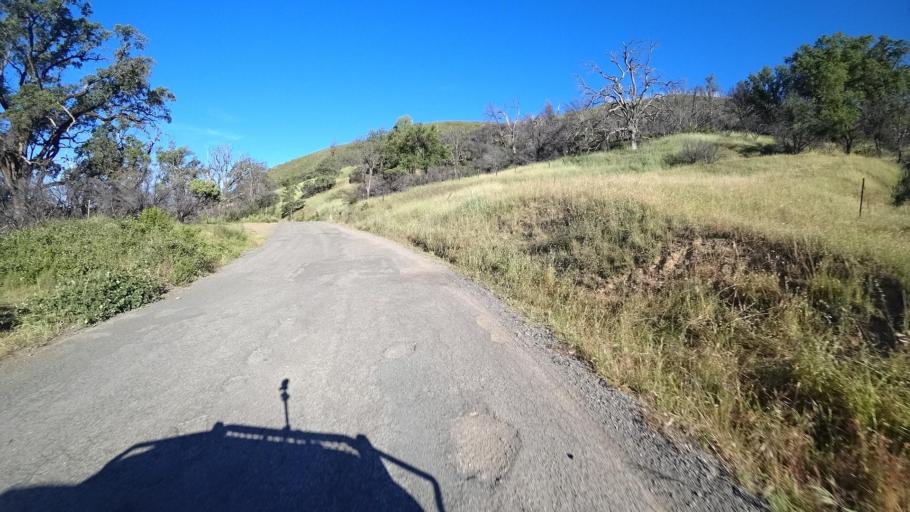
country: US
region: California
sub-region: Lake County
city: Upper Lake
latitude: 39.2657
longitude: -122.9282
